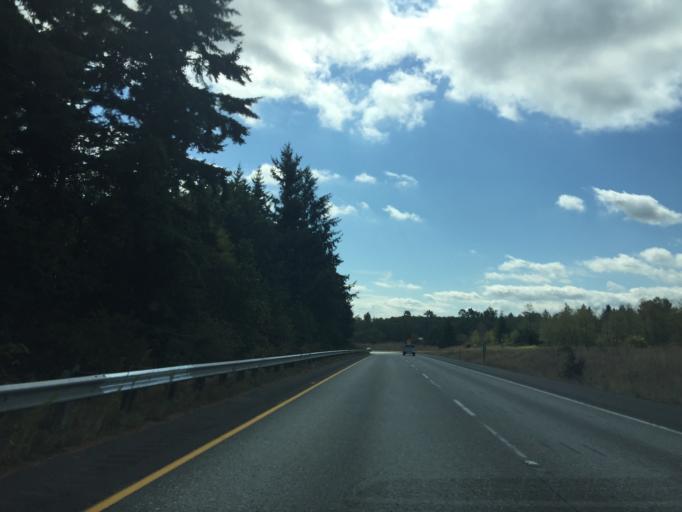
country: US
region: Washington
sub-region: Skagit County
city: Burlington
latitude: 48.5383
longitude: -122.3535
